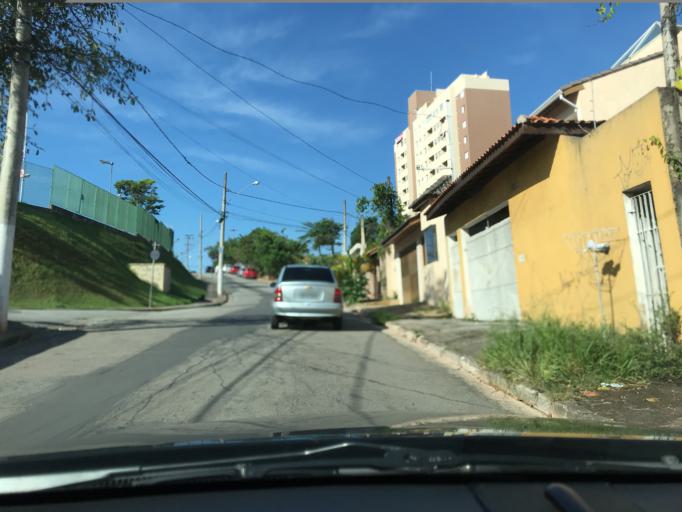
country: BR
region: Sao Paulo
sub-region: Itapevi
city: Itapevi
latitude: -23.5366
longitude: -46.9427
